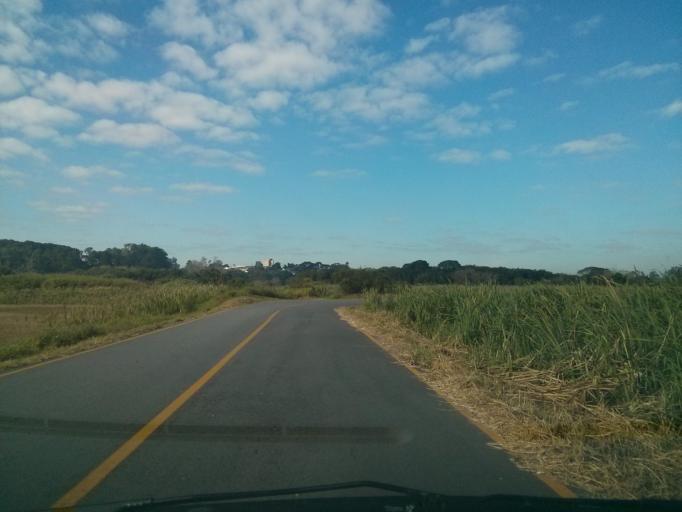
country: BR
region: Parana
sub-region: Sao Jose Dos Pinhais
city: Sao Jose dos Pinhais
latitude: -25.5306
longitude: -49.2234
